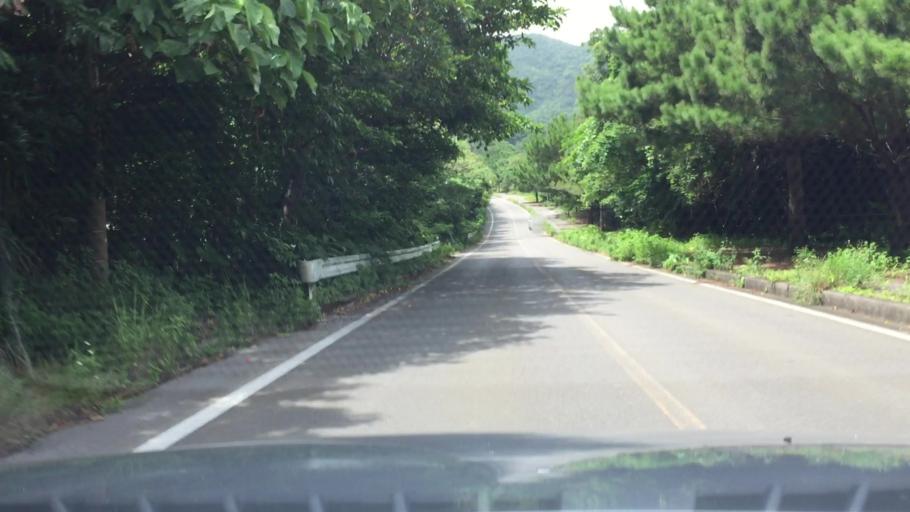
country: JP
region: Okinawa
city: Ishigaki
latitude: 24.4278
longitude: 124.2107
